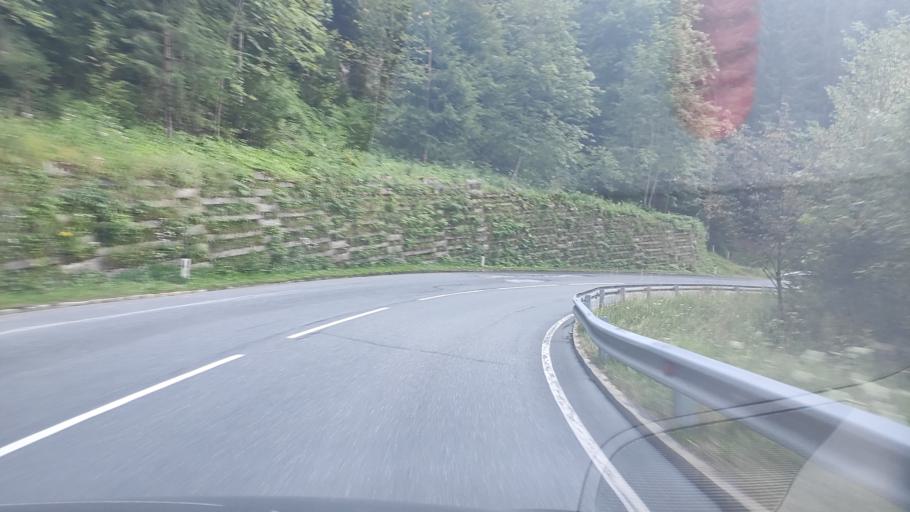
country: AT
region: Salzburg
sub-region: Politischer Bezirk Zell am See
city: Taxenbach
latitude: 47.2855
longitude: 12.9556
